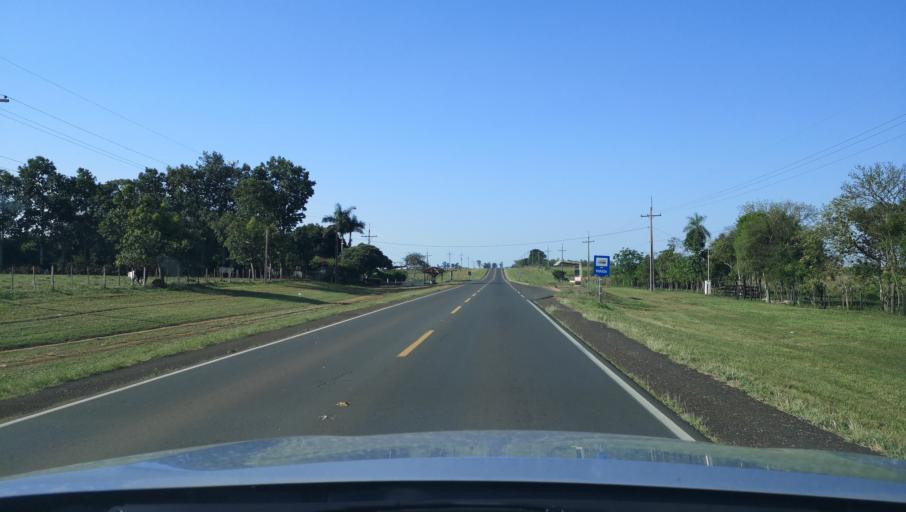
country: PY
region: Misiones
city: Santa Maria
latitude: -26.8164
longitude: -57.0243
